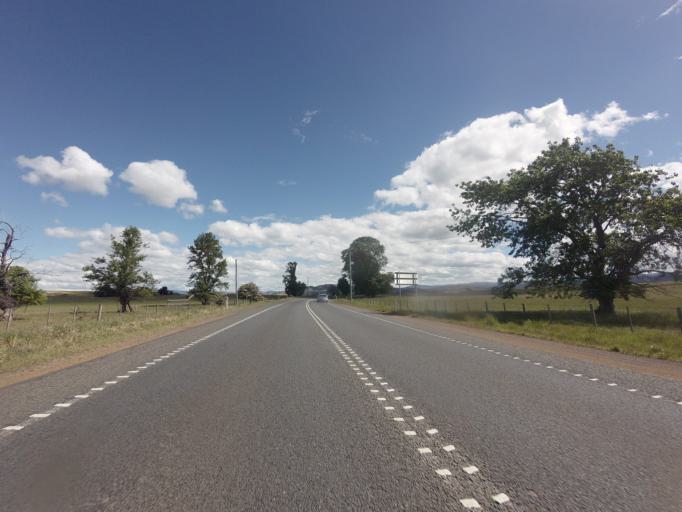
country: AU
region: Tasmania
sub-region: Northern Midlands
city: Evandale
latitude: -42.0057
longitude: 147.4983
